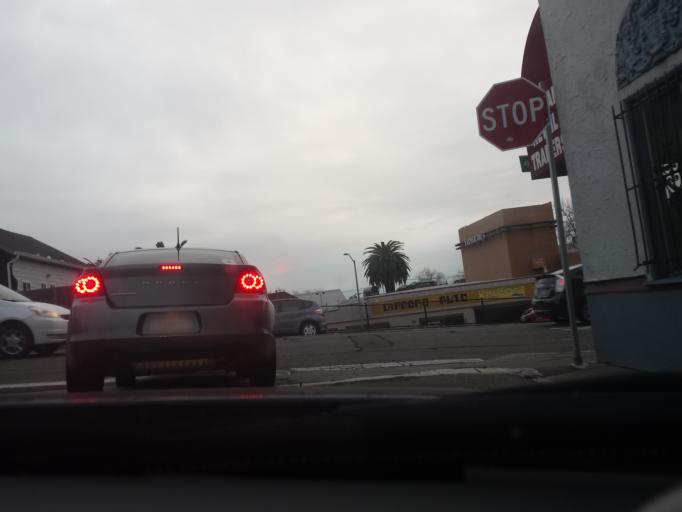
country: US
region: California
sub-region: Alameda County
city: Piedmont
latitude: 37.8002
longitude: -122.2150
